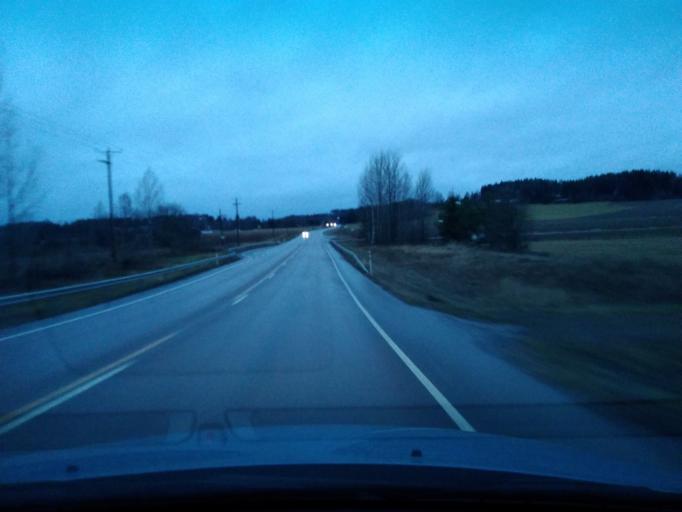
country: FI
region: Uusimaa
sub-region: Porvoo
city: Askola
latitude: 60.4520
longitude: 25.5838
